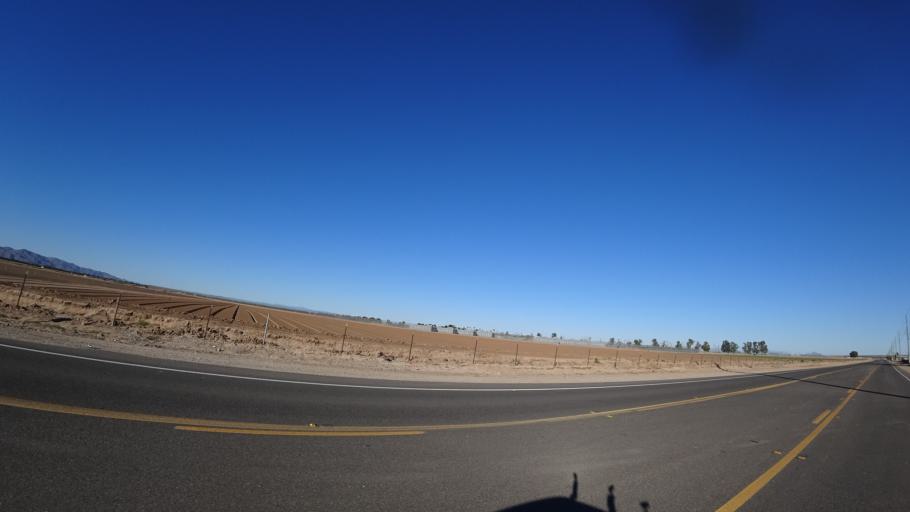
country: US
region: Arizona
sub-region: Maricopa County
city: Citrus Park
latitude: 33.4646
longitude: -112.4510
